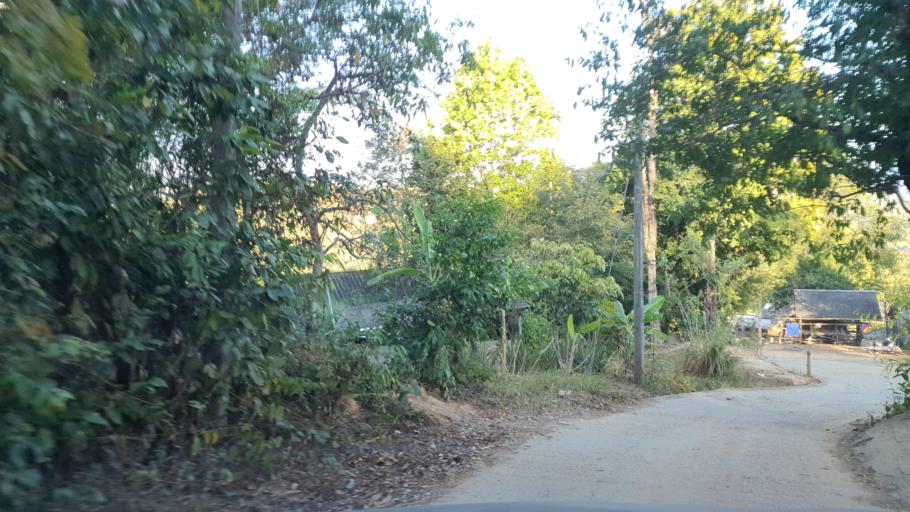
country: TH
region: Chiang Mai
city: Mae Wang
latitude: 18.6583
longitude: 98.6345
